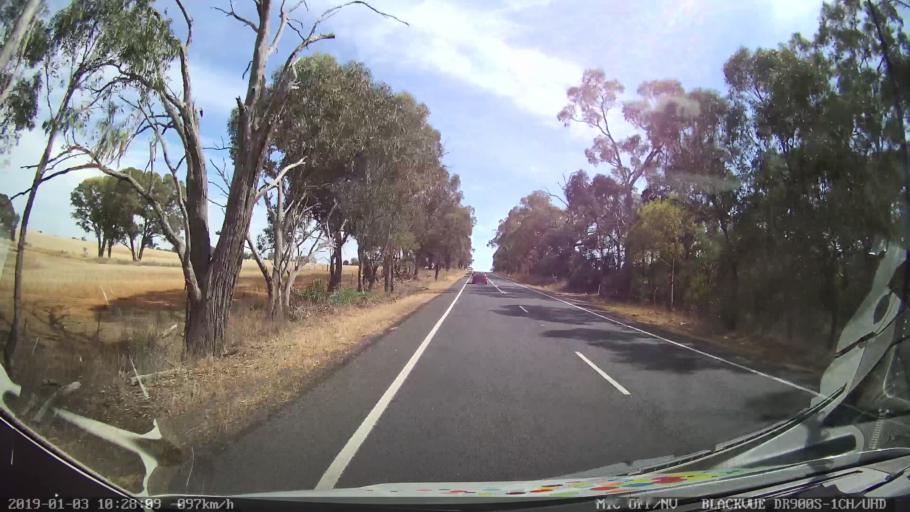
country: AU
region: New South Wales
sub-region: Young
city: Young
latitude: -34.3919
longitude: 148.2586
